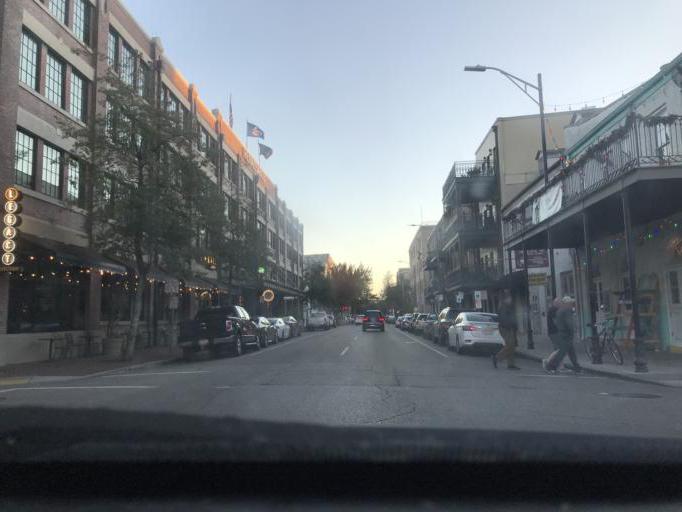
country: US
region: Louisiana
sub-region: Orleans Parish
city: New Orleans
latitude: 29.9466
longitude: -90.0673
